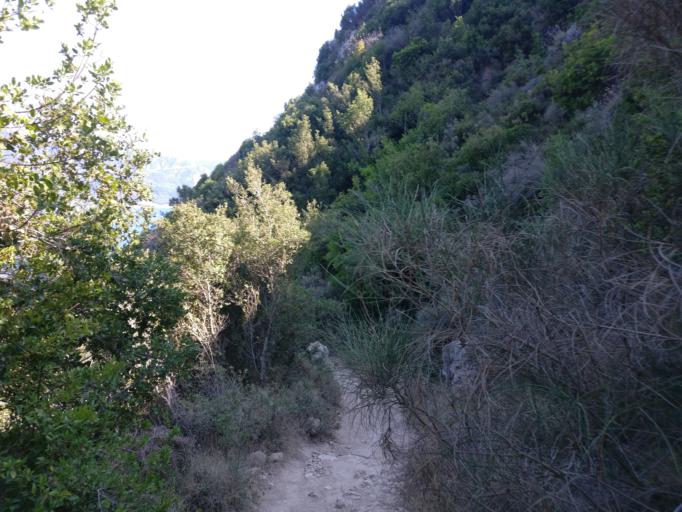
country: GR
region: Ionian Islands
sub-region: Nomos Kerkyras
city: Agios Georgis
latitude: 39.7171
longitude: 19.6583
